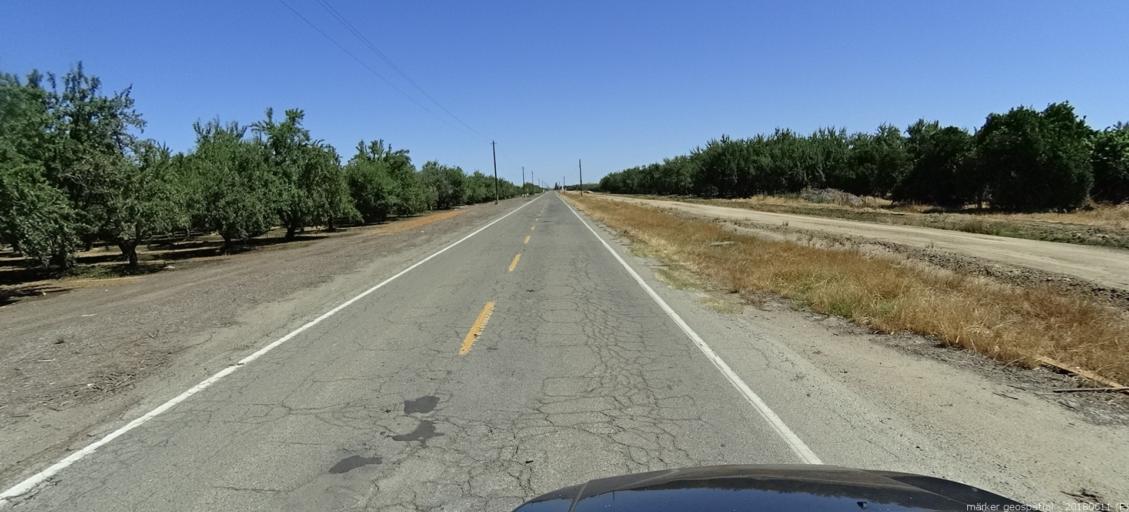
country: US
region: California
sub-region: Madera County
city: Fairmead
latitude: 37.0522
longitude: -120.2024
